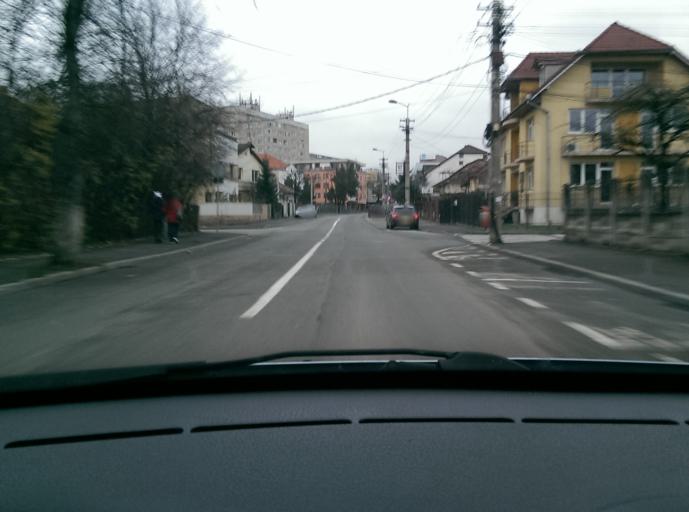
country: RO
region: Cluj
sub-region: Municipiul Cluj-Napoca
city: Cluj-Napoca
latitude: 46.7653
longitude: 23.6112
